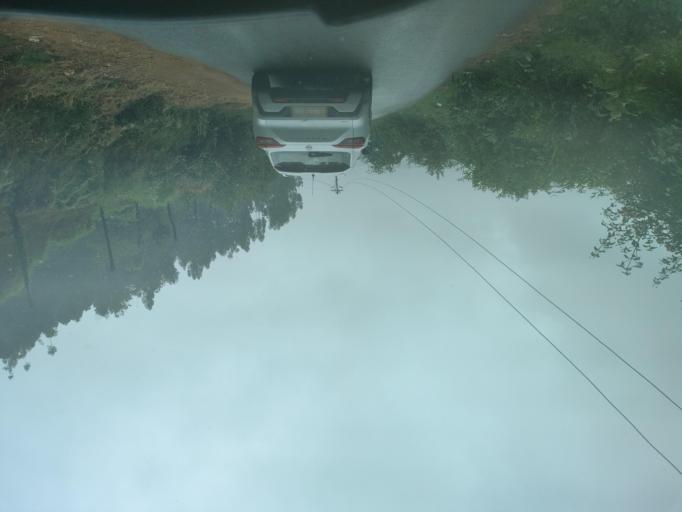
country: IN
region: Tamil Nadu
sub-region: Dindigul
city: Kodaikanal
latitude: 10.2371
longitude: 77.3495
